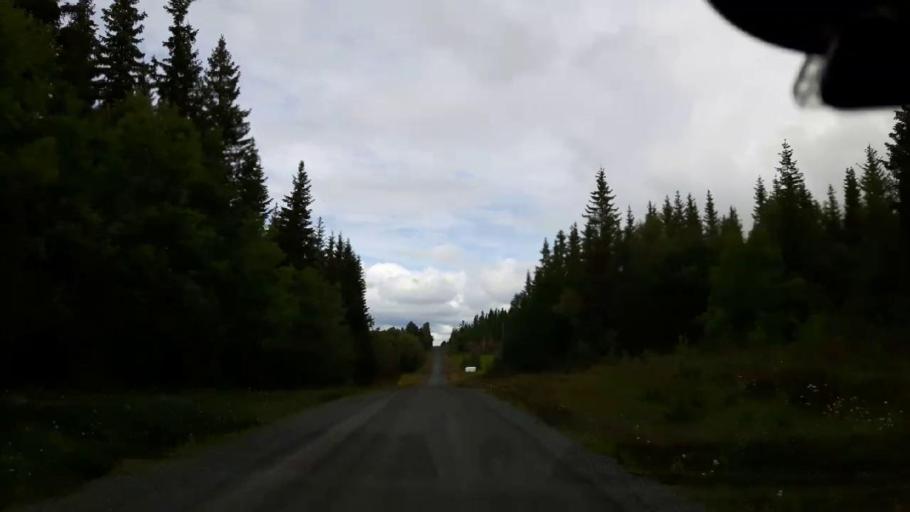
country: SE
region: Jaemtland
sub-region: Krokoms Kommun
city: Valla
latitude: 63.5057
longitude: 13.9582
